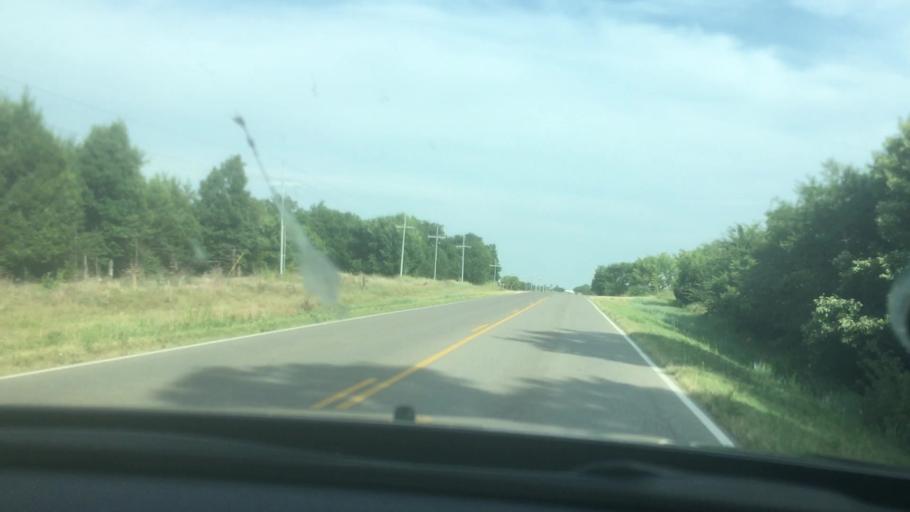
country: US
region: Oklahoma
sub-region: Pontotoc County
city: Ada
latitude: 34.7911
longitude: -96.8045
